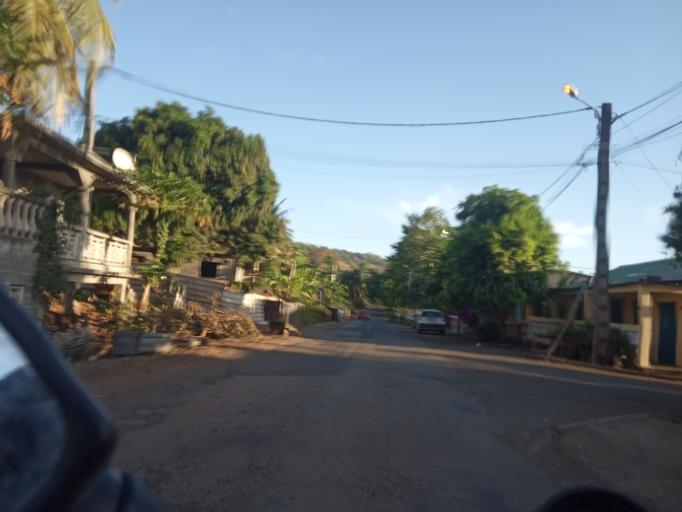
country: YT
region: Kani-Keli
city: Kani Keli
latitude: -12.9289
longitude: 45.1040
